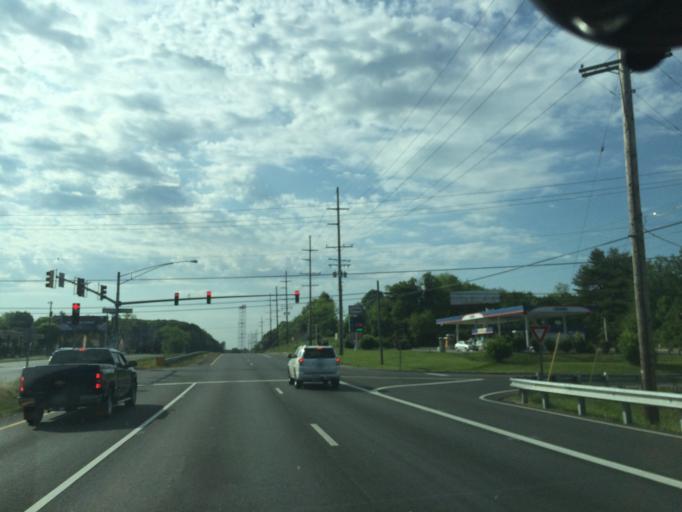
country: US
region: Maryland
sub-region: Carroll County
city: Westminster
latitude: 39.5260
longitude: -76.9224
